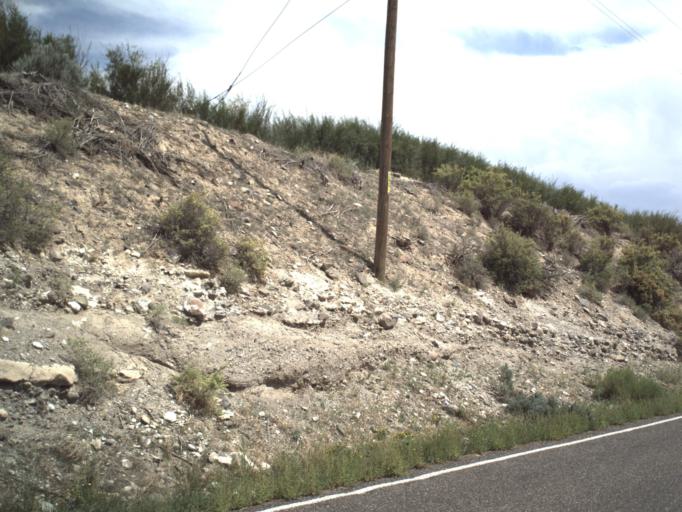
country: US
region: Utah
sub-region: Piute County
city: Junction
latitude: 38.1150
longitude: -111.9937
